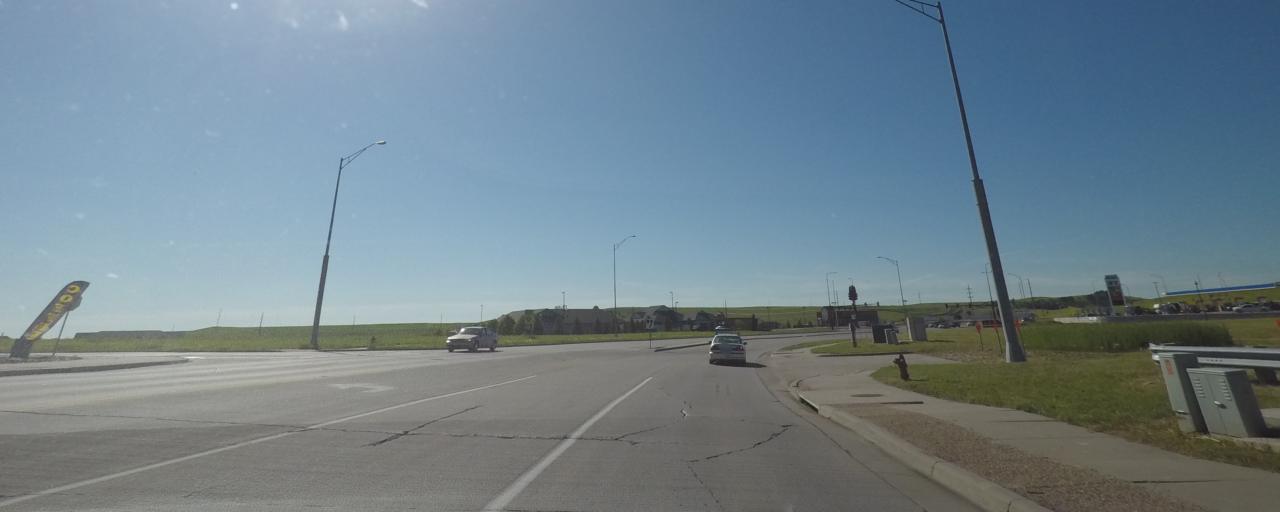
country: US
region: South Dakota
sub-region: Pennington County
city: Rapid City
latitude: 44.0345
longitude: -103.2134
